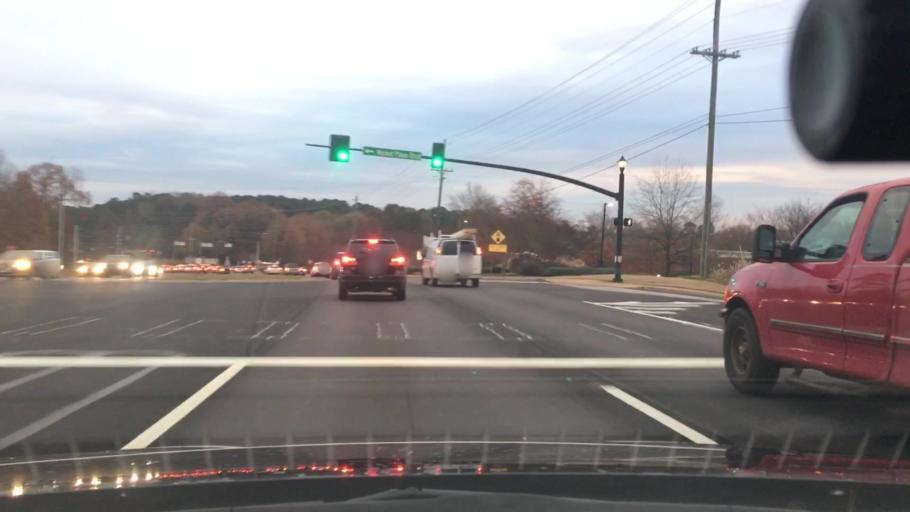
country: US
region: Georgia
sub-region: Fayette County
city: Peachtree City
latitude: 33.3966
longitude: -84.5941
